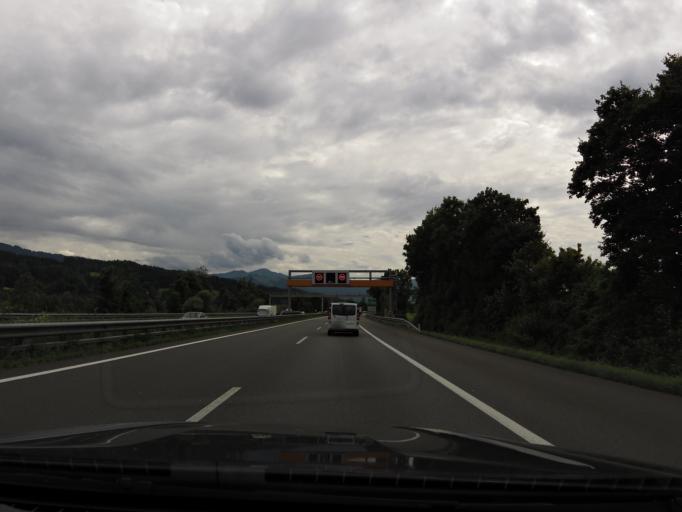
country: AT
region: Tyrol
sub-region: Politischer Bezirk Kufstein
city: Schwoich
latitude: 47.5465
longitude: 12.1179
